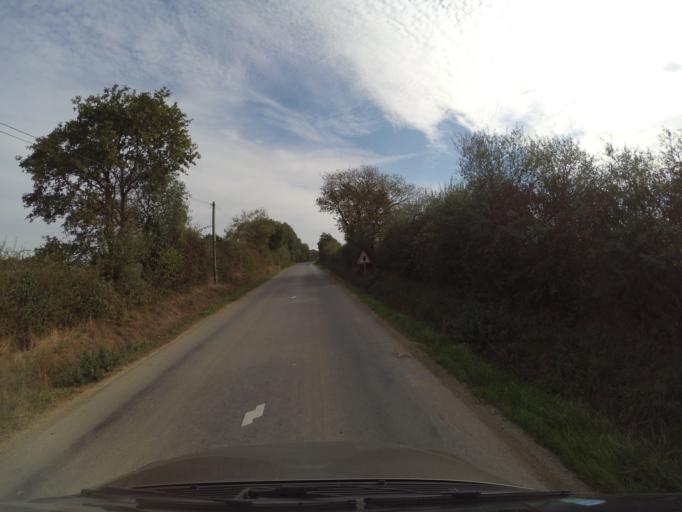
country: FR
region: Pays de la Loire
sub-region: Departement de Maine-et-Loire
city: Villedieu-la-Blouere
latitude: 47.1546
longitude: -1.0417
